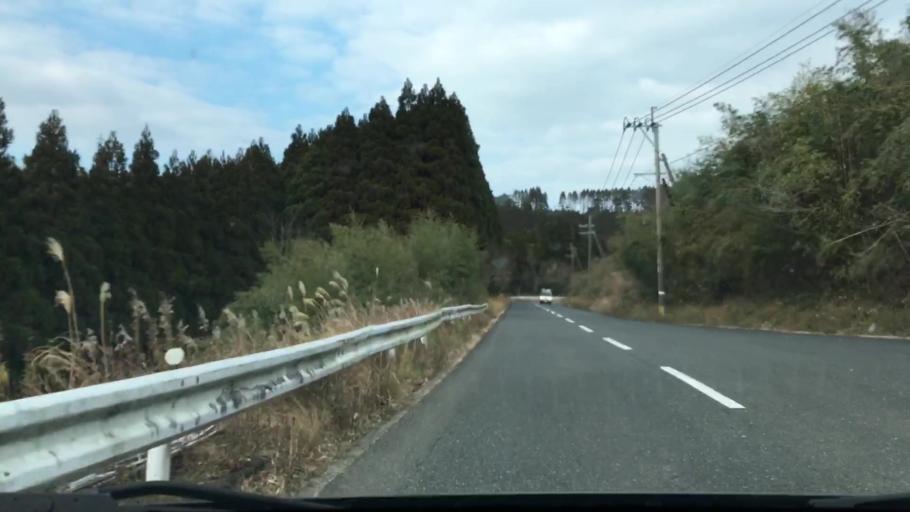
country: JP
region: Miyazaki
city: Nichinan
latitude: 31.6651
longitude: 131.3177
